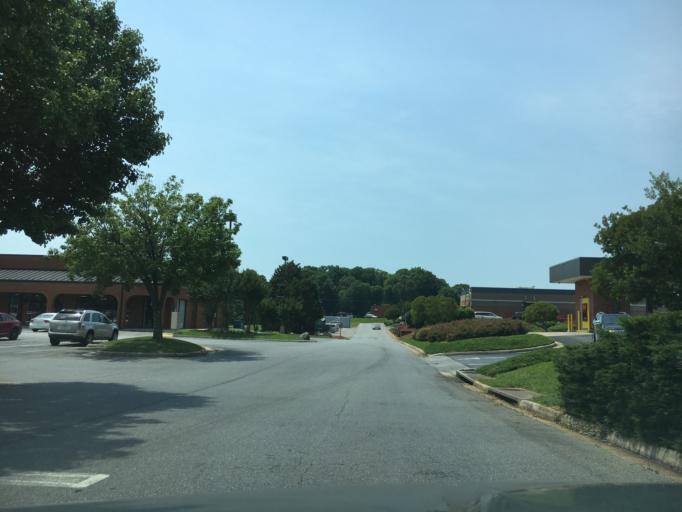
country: US
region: Virginia
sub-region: Bedford County
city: Forest
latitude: 37.3773
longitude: -79.2478
